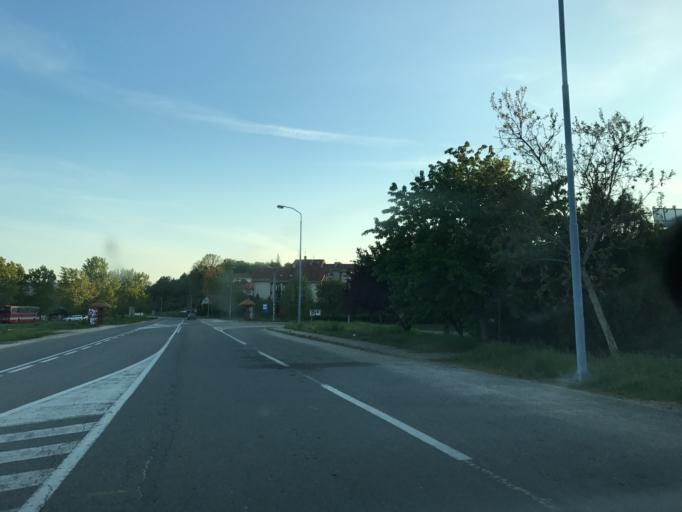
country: RO
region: Mehedinti
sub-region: Comuna Gogosu
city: Ostrovu Mare
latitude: 44.4832
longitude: 22.4555
